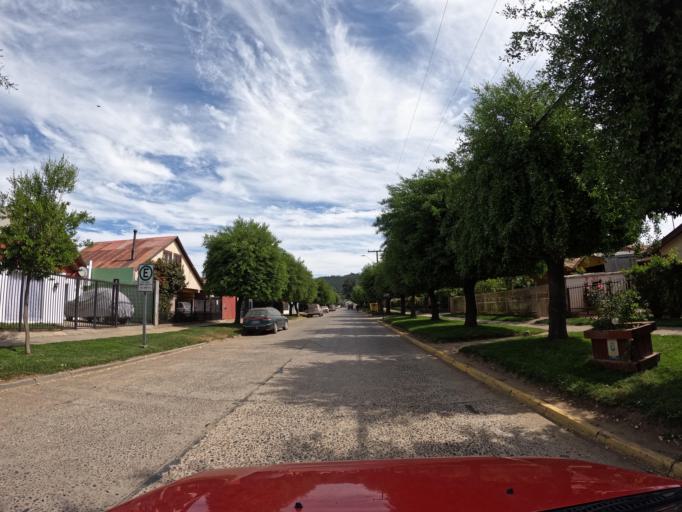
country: CL
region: Maule
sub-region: Provincia de Talca
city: Constitucion
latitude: -35.0894
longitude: -72.0212
